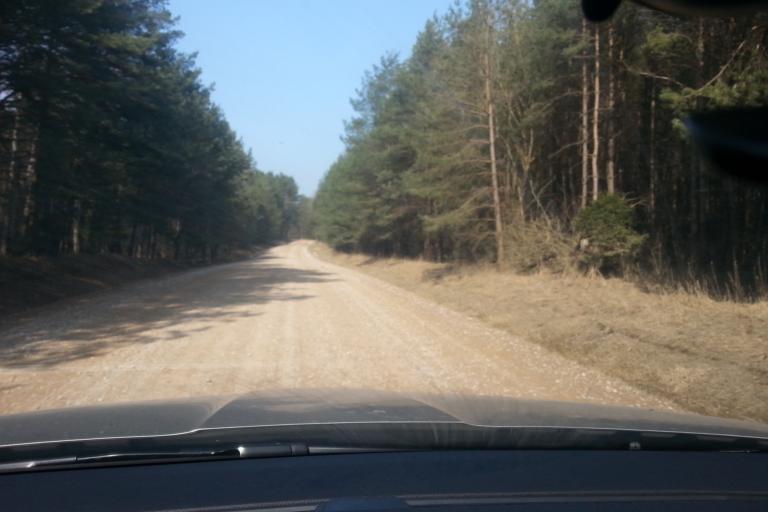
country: LT
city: Trakai
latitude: 54.5611
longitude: 24.9787
